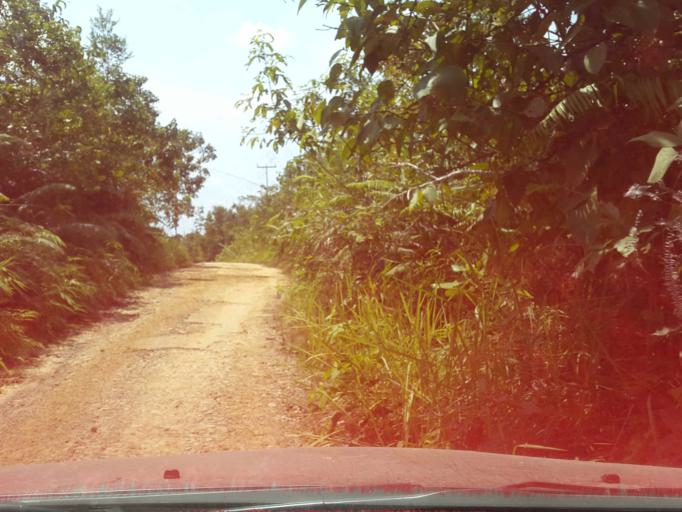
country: MY
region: Sarawak
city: Simanggang
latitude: 0.8483
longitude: 111.7752
